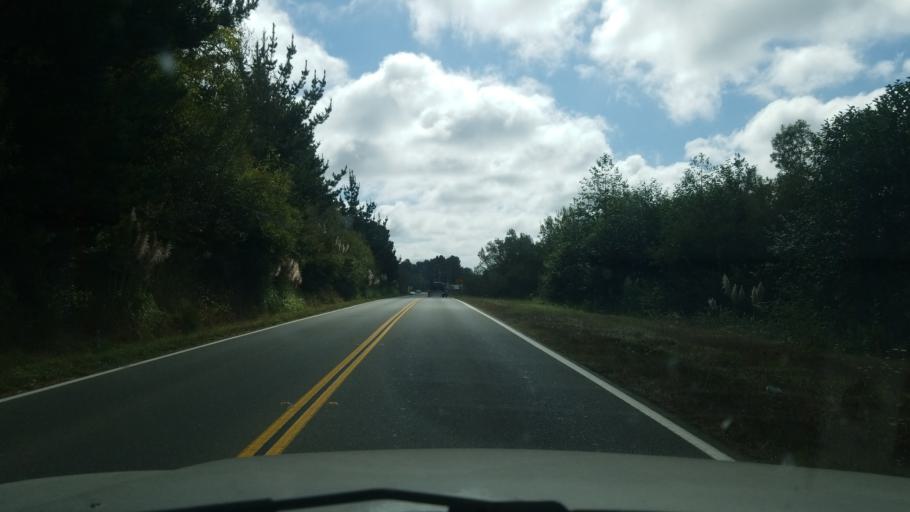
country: US
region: California
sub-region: Humboldt County
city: Fortuna
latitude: 40.6182
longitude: -124.2057
